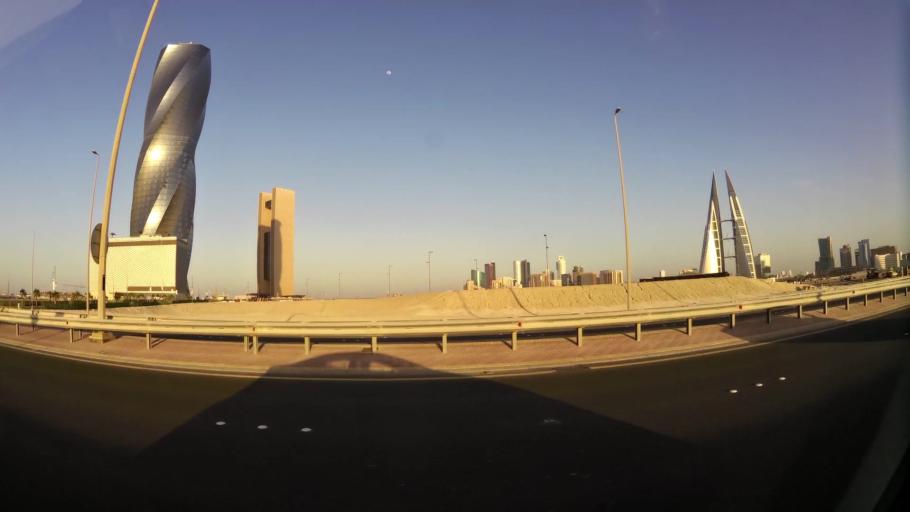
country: BH
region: Manama
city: Manama
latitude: 26.2448
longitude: 50.5743
